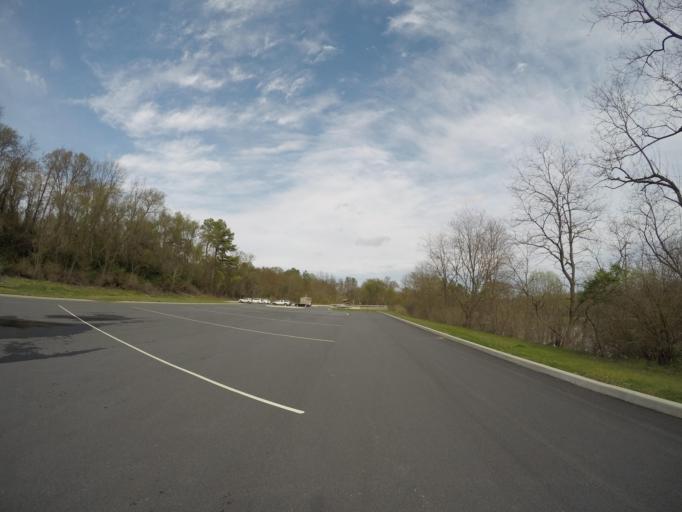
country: US
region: Delaware
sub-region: New Castle County
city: Glasgow
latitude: 39.5443
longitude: -75.7207
